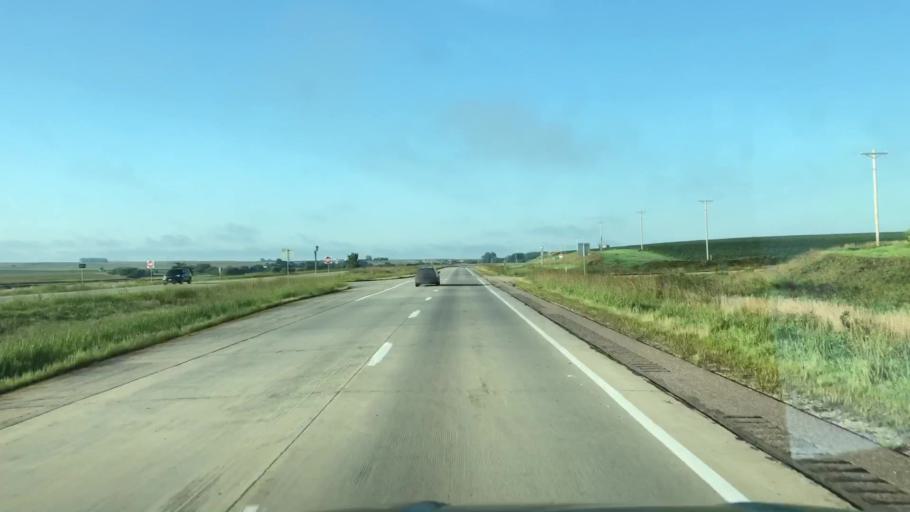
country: US
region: Iowa
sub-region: Sioux County
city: Alton
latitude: 42.9397
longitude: -96.0439
